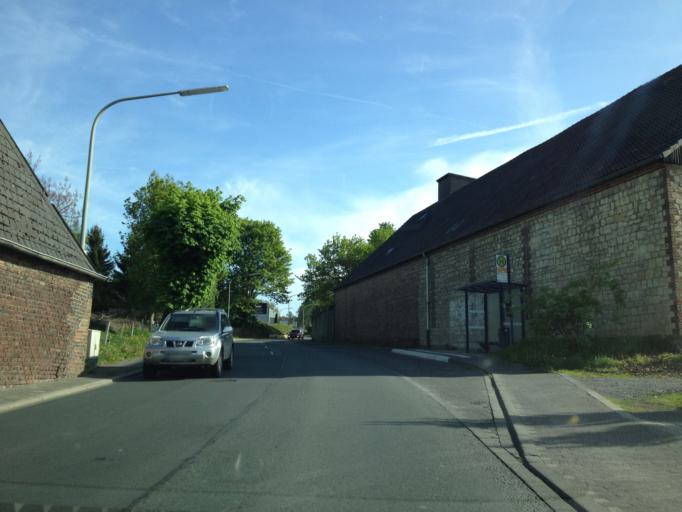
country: DE
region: North Rhine-Westphalia
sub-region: Regierungsbezirk Arnsberg
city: Werl
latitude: 51.4871
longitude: 7.9708
